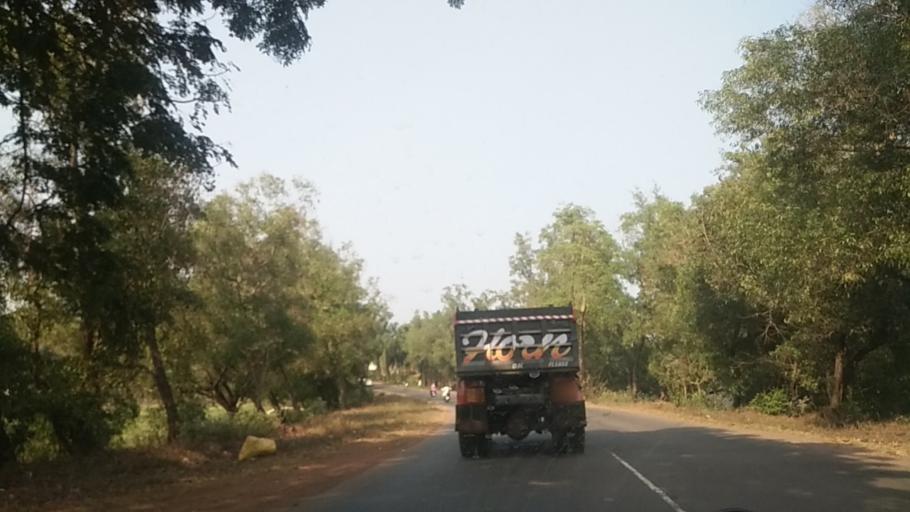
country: IN
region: Goa
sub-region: North Goa
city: Colovale
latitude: 15.6557
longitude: 73.8391
